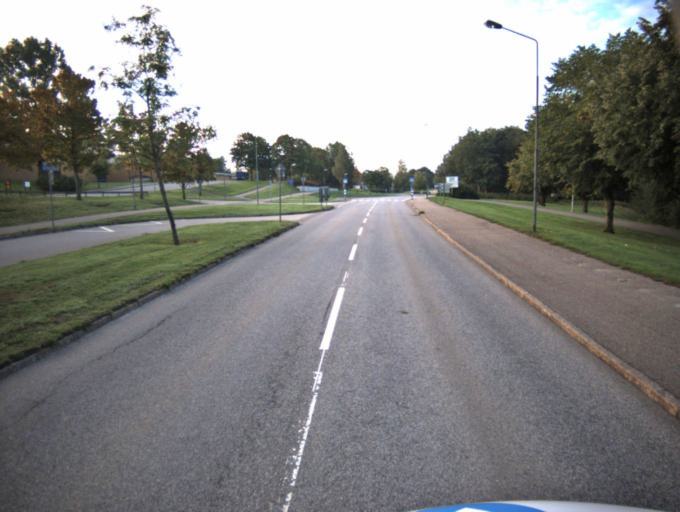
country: SE
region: Vaestra Goetaland
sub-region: Ulricehamns Kommun
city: Ulricehamn
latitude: 57.7905
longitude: 13.4263
